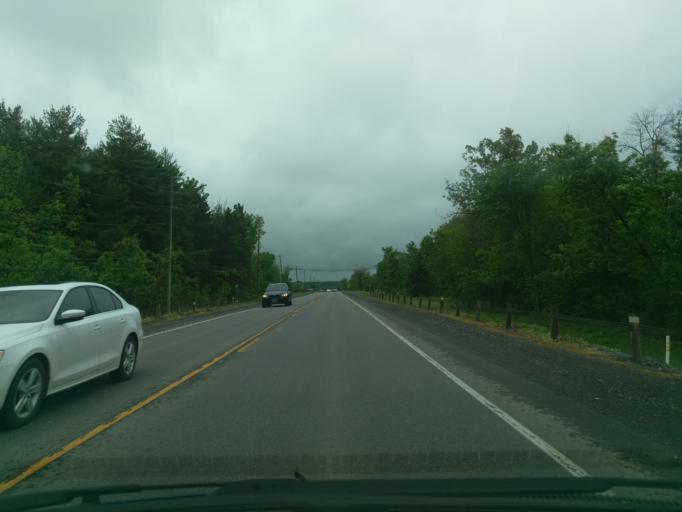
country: CA
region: Ontario
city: Clarence-Rockland
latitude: 45.5316
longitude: -75.3142
